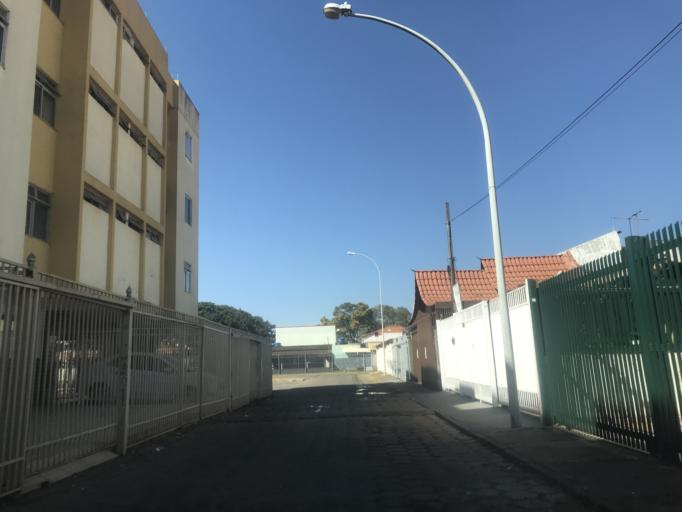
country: BR
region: Federal District
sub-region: Brasilia
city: Brasilia
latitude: -15.8169
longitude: -47.9876
